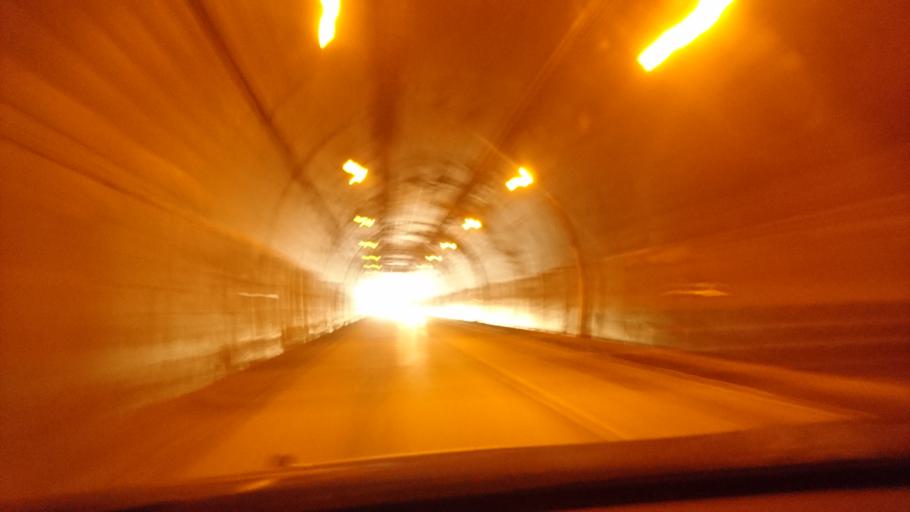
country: JP
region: Iwate
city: Miyako
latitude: 39.6902
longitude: 141.9508
